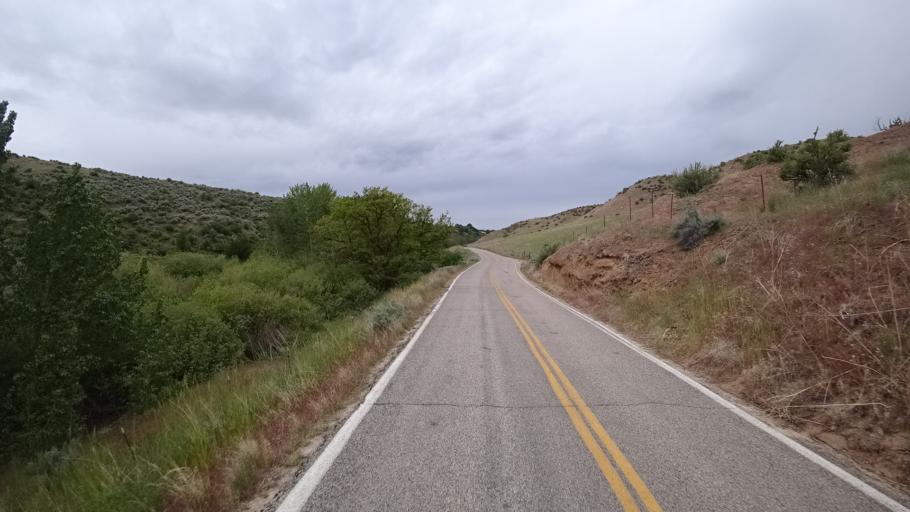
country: US
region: Idaho
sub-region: Ada County
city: Boise
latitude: 43.6167
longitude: -116.1507
